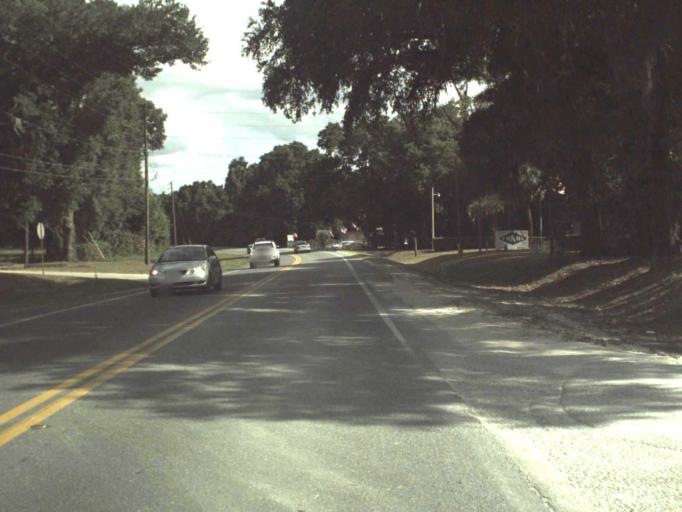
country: US
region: Florida
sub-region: Marion County
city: Belleview
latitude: 29.0698
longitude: -82.0536
